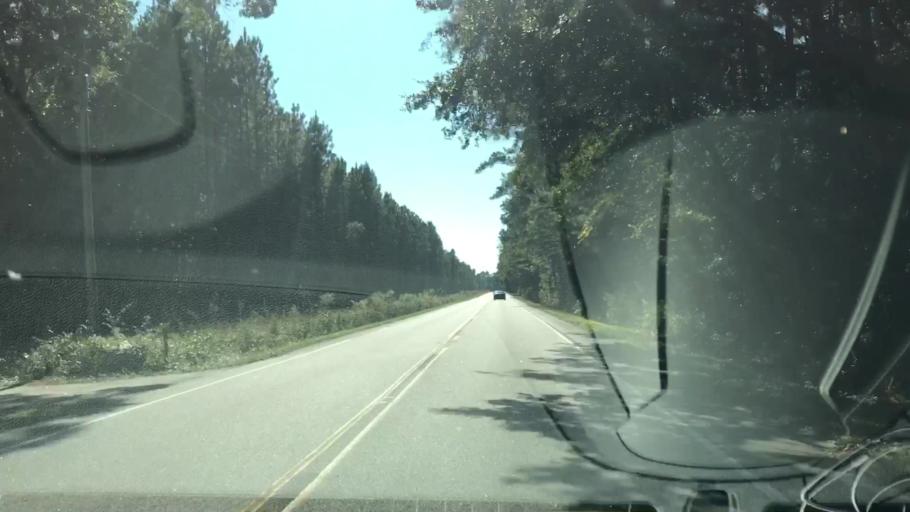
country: US
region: South Carolina
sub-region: Jasper County
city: Ridgeland
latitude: 32.5053
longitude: -80.8871
